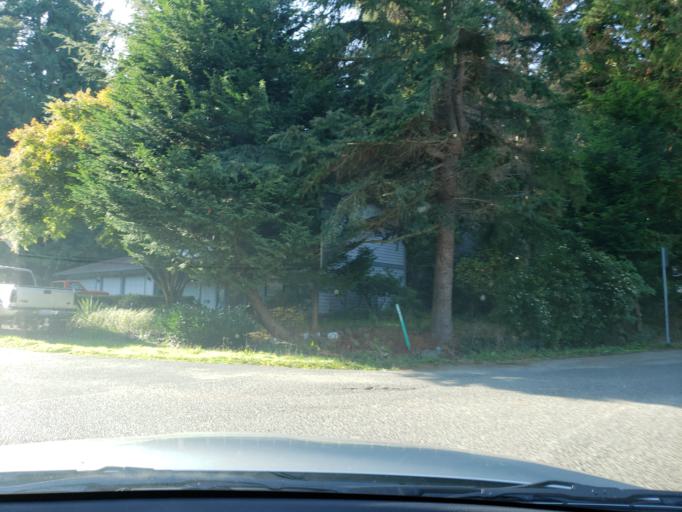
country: US
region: Washington
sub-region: Snohomish County
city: Meadowdale
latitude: 47.8692
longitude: -122.3150
